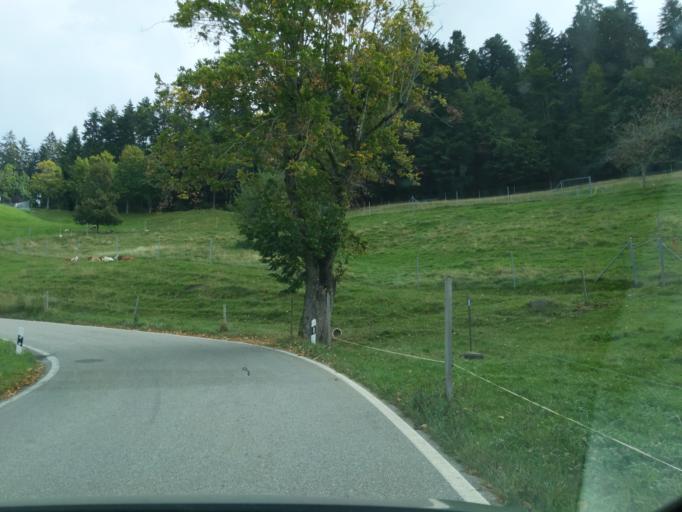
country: CH
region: Bern
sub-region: Oberaargau
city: Wyssachen
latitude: 47.0597
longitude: 7.8362
